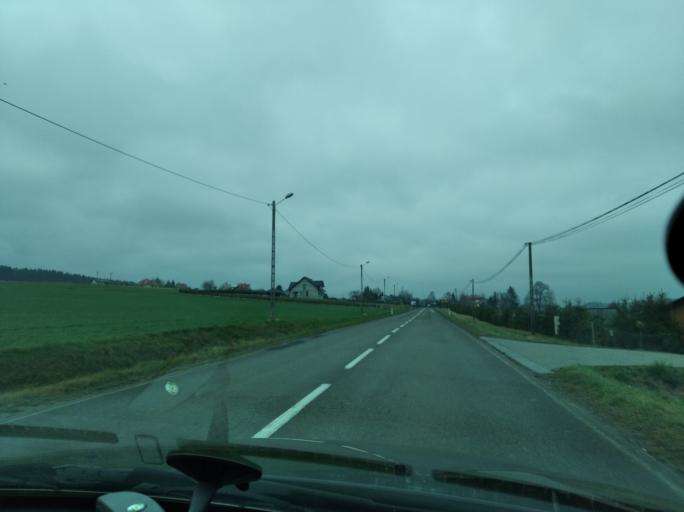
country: PL
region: Subcarpathian Voivodeship
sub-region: Powiat rzeszowski
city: Dynow
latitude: 49.8599
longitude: 22.2487
